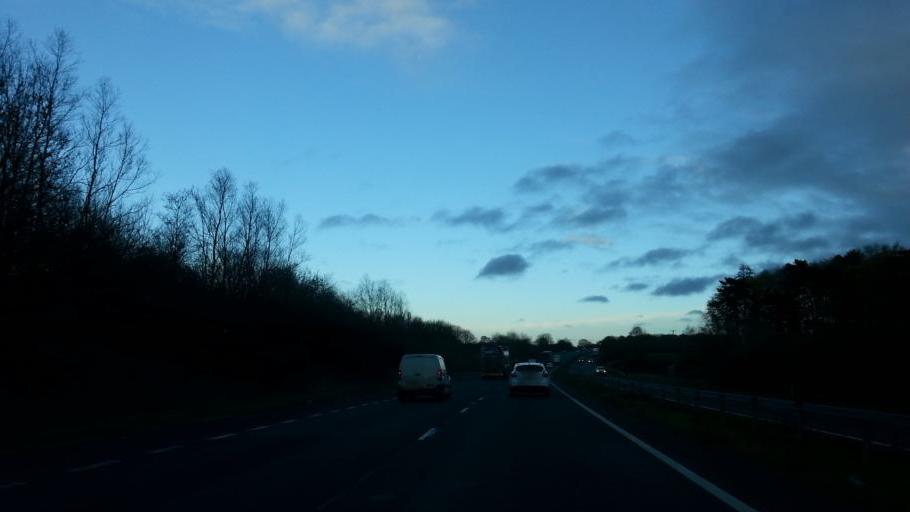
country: GB
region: England
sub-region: Northamptonshire
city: Silverstone
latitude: 52.0659
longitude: -1.0720
